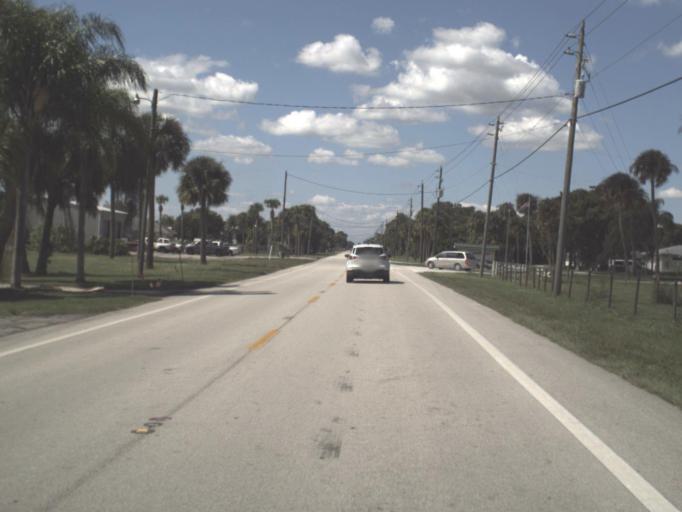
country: US
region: Florida
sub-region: Okeechobee County
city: Taylor Creek
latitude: 27.1872
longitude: -80.7440
